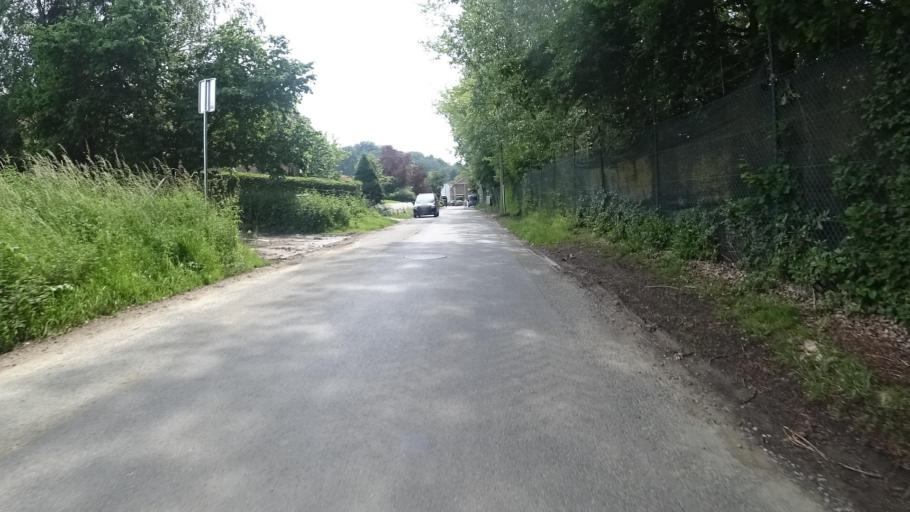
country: BE
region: Wallonia
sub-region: Province du Brabant Wallon
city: Wavre
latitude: 50.6975
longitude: 4.5928
